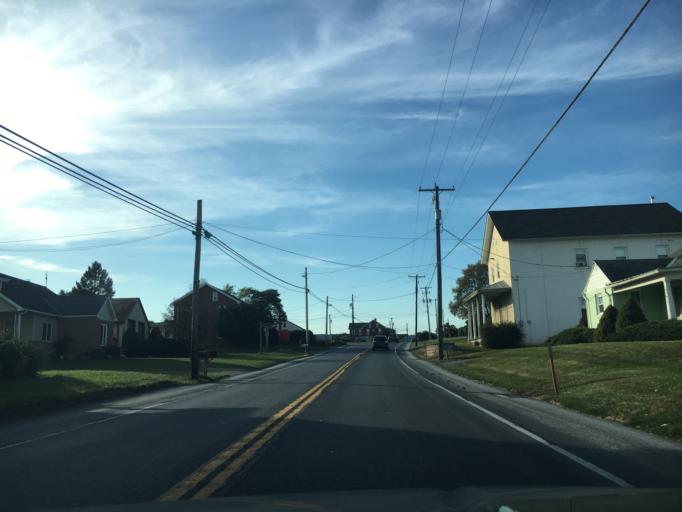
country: US
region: Pennsylvania
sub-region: Lancaster County
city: New Holland
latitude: 40.1470
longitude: -76.1196
